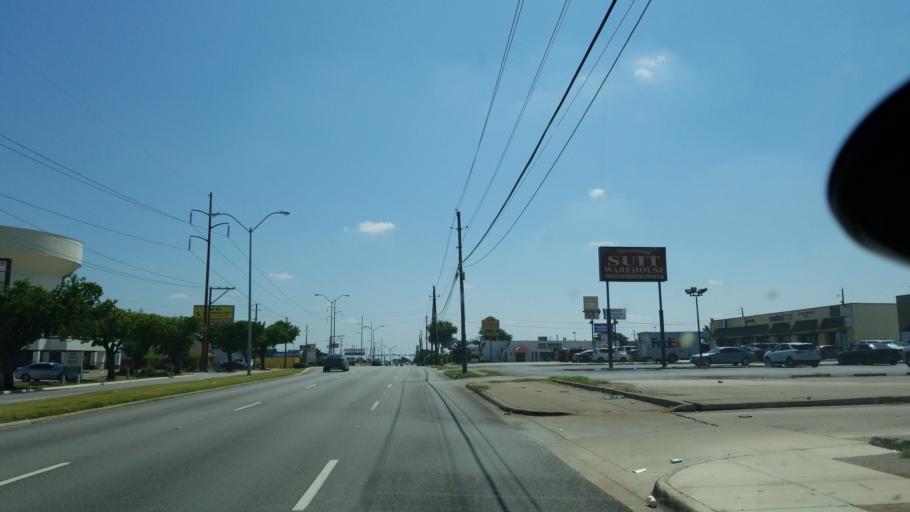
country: US
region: Texas
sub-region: Dallas County
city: Duncanville
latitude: 32.6618
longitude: -96.8865
